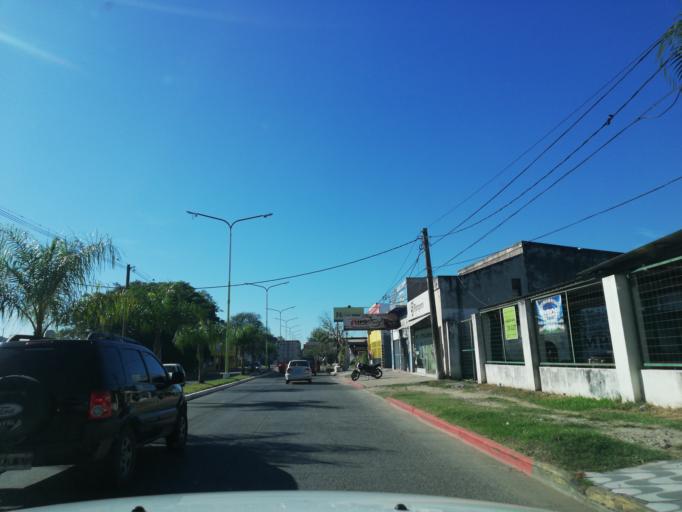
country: AR
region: Corrientes
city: Corrientes
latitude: -27.4754
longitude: -58.7965
